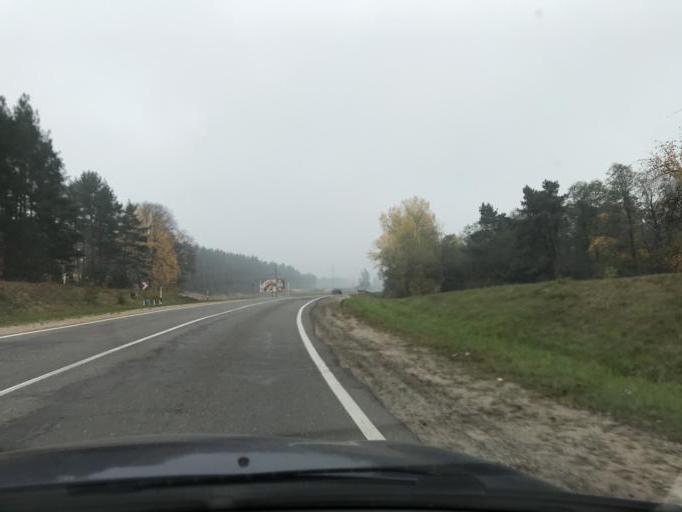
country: BY
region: Grodnenskaya
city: Hrodna
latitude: 53.8102
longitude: 23.8624
